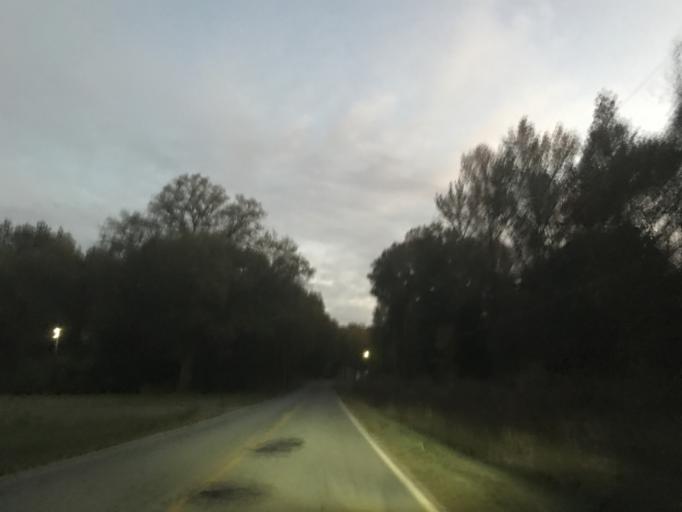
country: US
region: South Carolina
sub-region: Spartanburg County
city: Mayo
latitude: 35.0541
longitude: -81.8910
